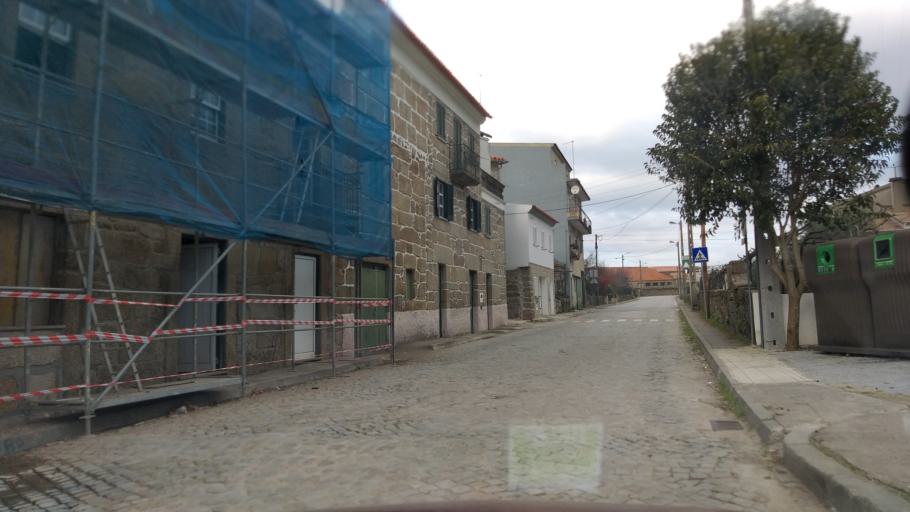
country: PT
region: Guarda
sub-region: Seia
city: Seia
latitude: 40.4954
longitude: -7.6262
